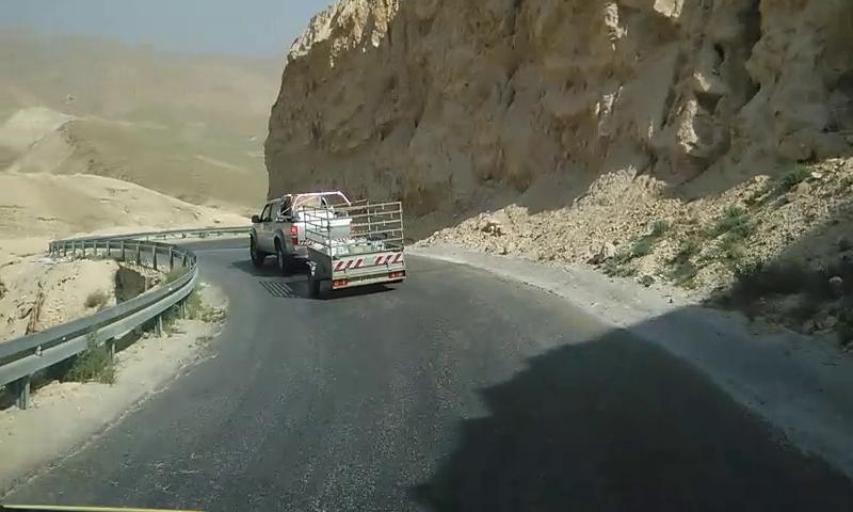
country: PS
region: West Bank
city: An Nuway`imah
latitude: 31.9160
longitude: 35.3867
